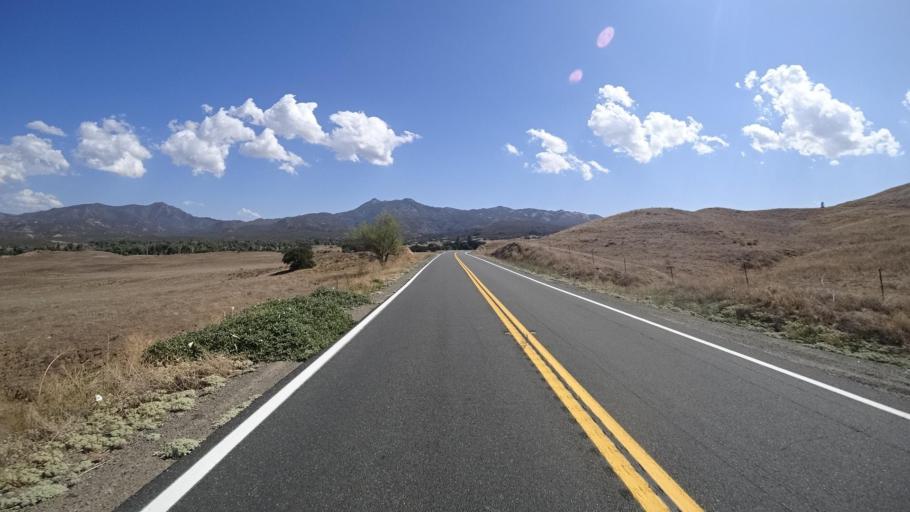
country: US
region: California
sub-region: San Diego County
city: Julian
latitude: 33.2711
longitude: -116.6520
